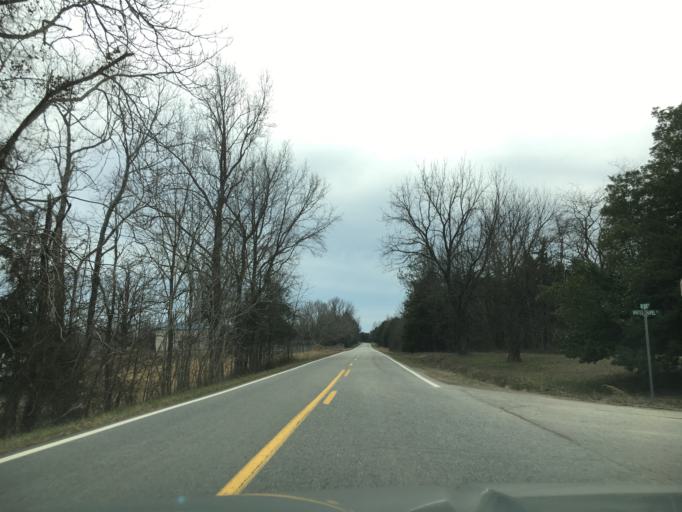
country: US
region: Virginia
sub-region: Charlotte County
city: Charlotte Court House
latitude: 37.1299
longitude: -78.7547
